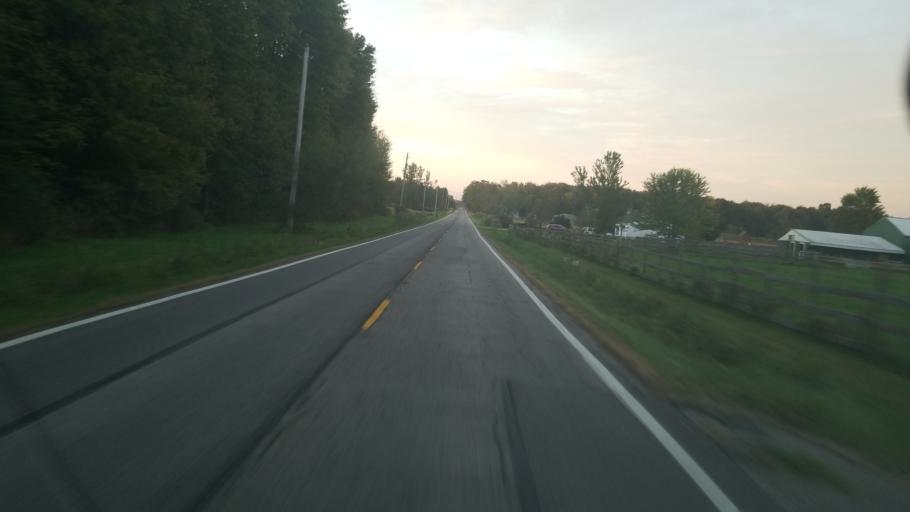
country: US
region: Ohio
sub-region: Ashtabula County
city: Andover
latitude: 41.6497
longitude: -80.6670
